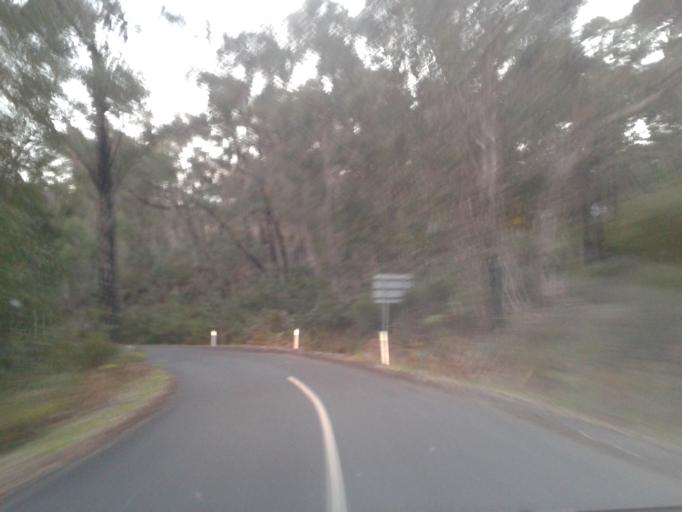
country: AU
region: Victoria
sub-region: Northern Grampians
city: Stawell
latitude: -37.1589
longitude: 142.4974
